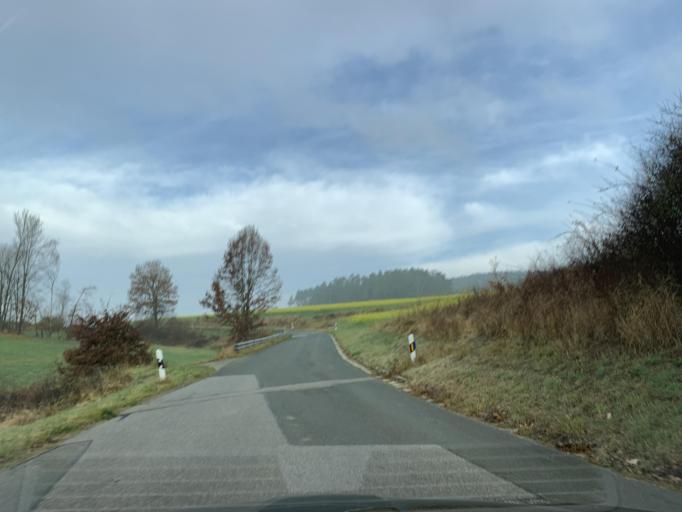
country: DE
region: Bavaria
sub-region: Upper Palatinate
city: Neunburg vorm Wald
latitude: 49.3669
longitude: 12.3936
